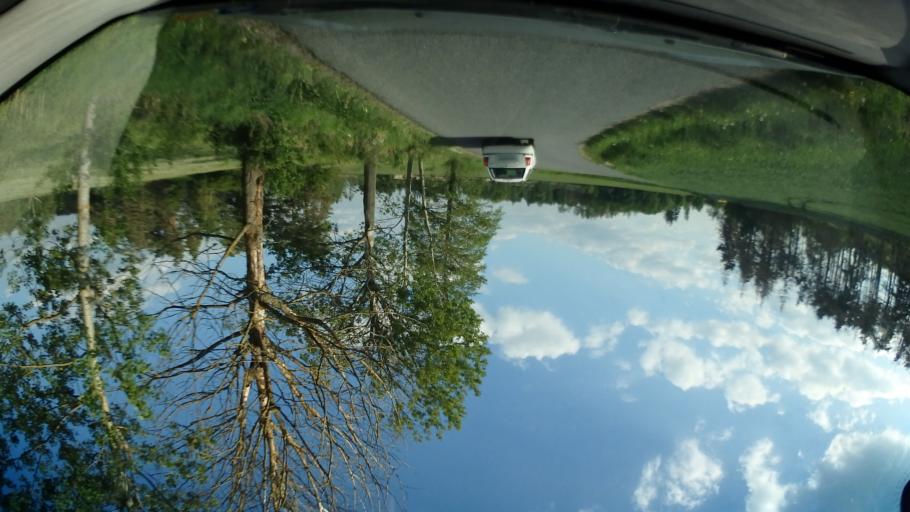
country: CZ
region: Vysocina
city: Budisov
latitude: 49.3075
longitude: 15.9776
